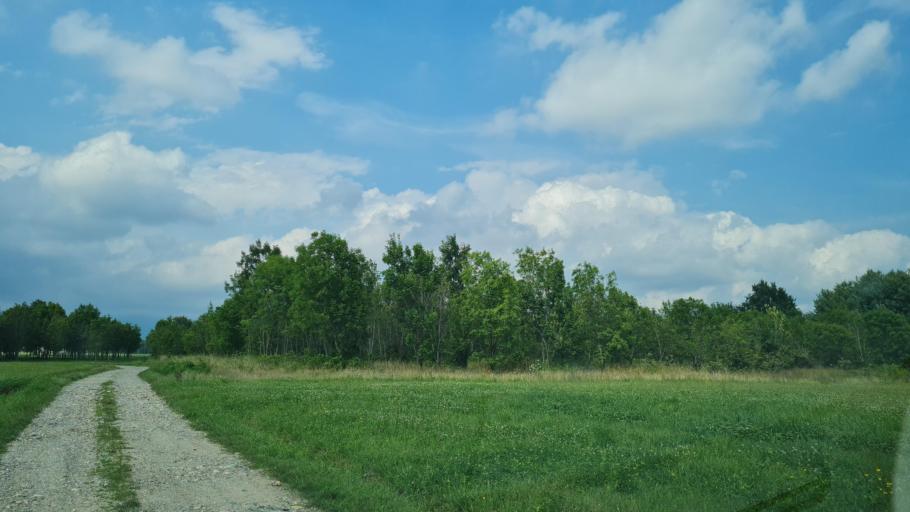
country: IT
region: Piedmont
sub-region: Provincia di Biella
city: Borriana
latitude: 45.5288
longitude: 8.0327
